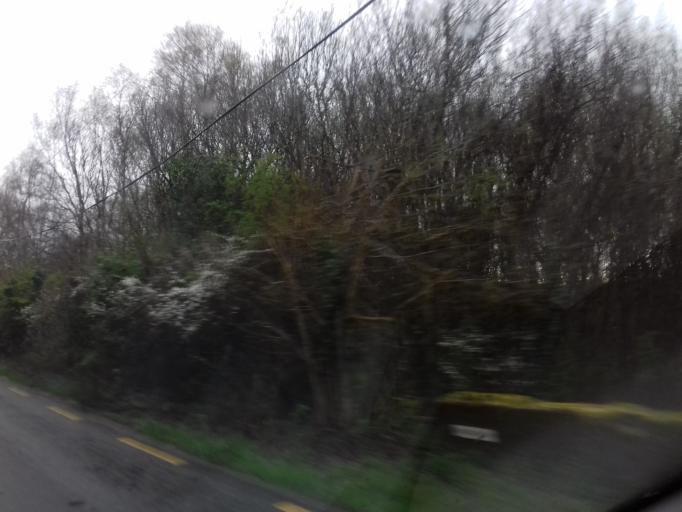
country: IE
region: Connaught
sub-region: County Leitrim
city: Manorhamilton
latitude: 54.2790
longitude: -7.9362
